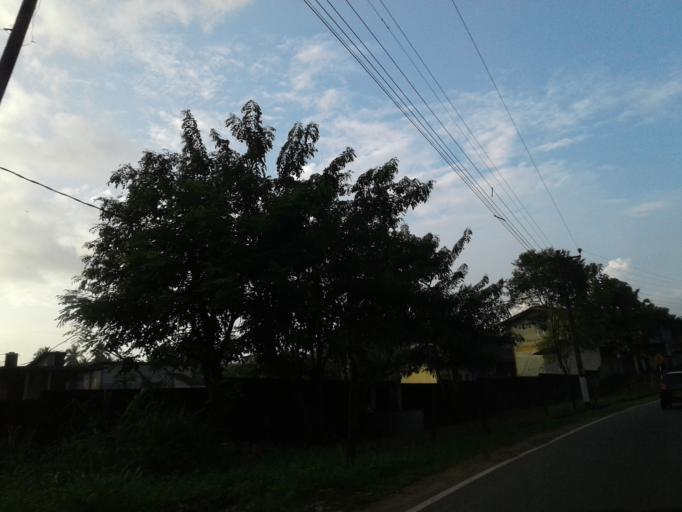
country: LK
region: Western
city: Kelaniya
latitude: 6.9710
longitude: 80.0022
